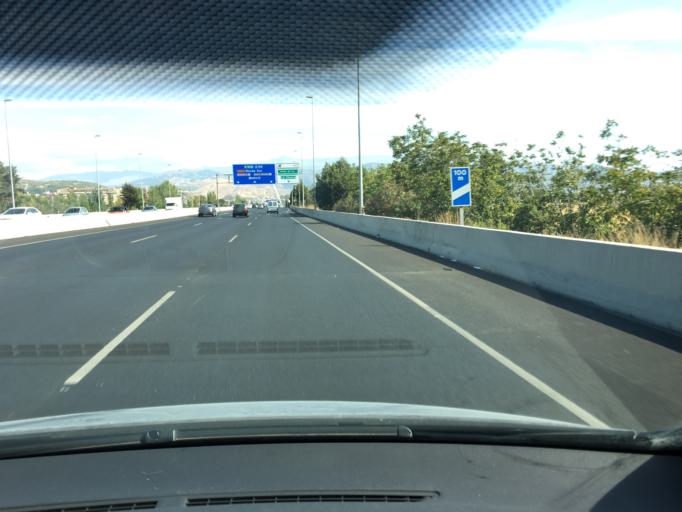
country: ES
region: Andalusia
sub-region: Provincia de Granada
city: Granada
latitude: 37.1846
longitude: -3.6291
